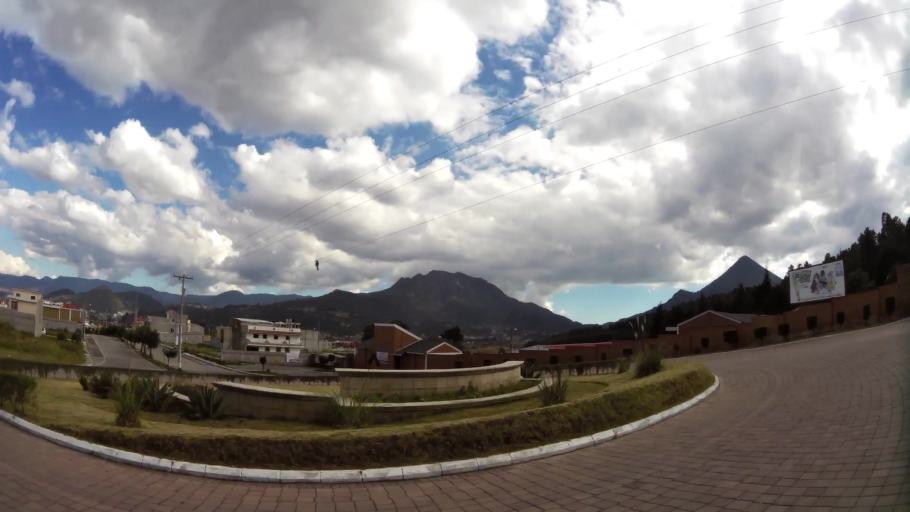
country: GT
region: Quetzaltenango
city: Quetzaltenango
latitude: 14.8353
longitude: -91.5524
